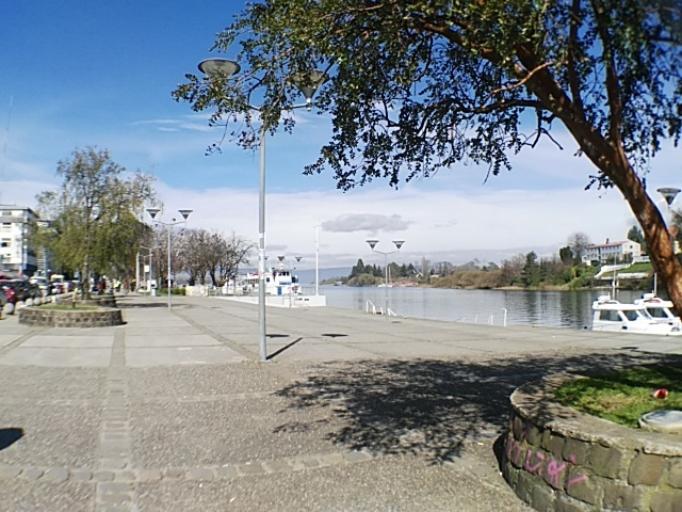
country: CL
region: Los Rios
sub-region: Provincia de Valdivia
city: Valdivia
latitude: -39.8142
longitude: -73.2487
